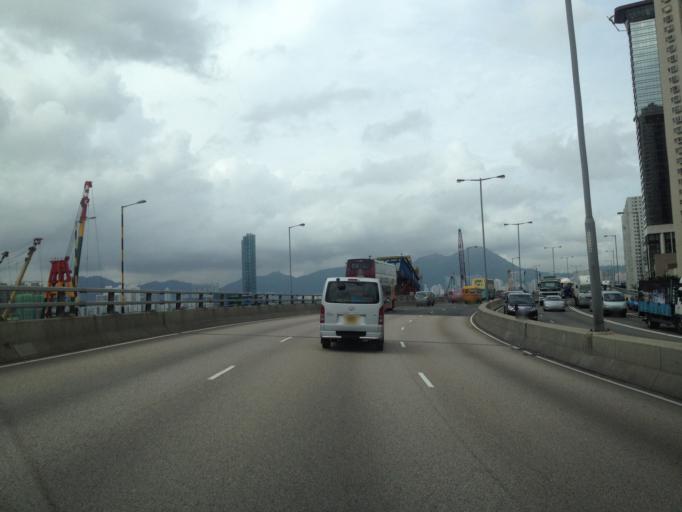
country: HK
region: Wanchai
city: Wan Chai
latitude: 22.2870
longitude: 114.1893
